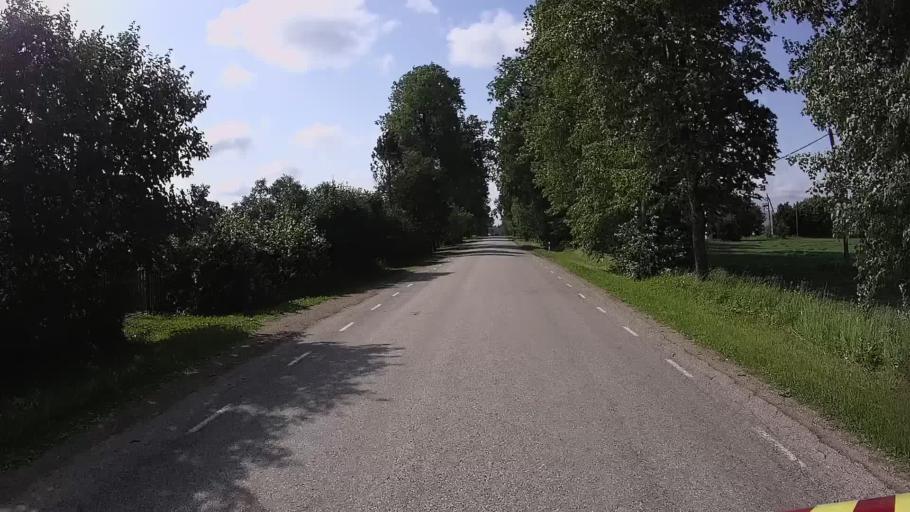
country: EE
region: Vorumaa
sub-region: Antsla vald
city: Vana-Antsla
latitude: 57.8668
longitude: 26.6086
